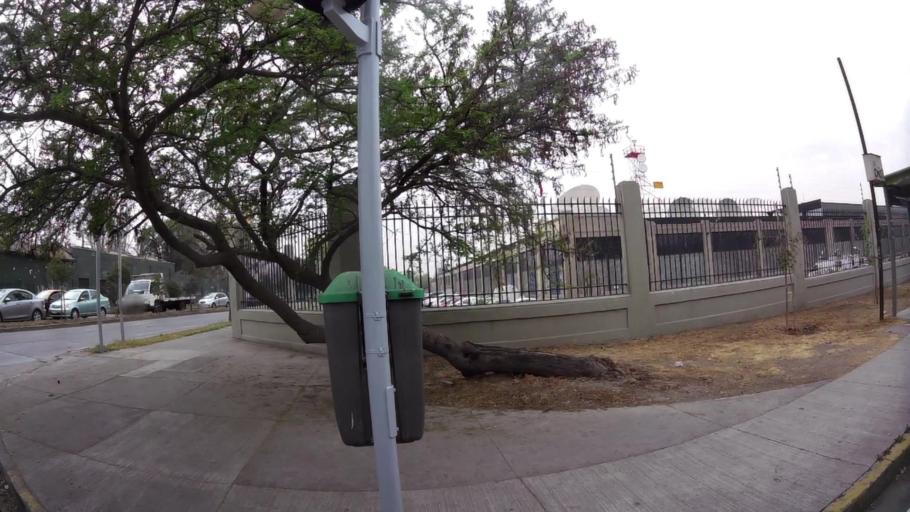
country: CL
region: Santiago Metropolitan
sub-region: Provincia de Santiago
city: Santiago
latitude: -33.4738
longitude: -70.6650
